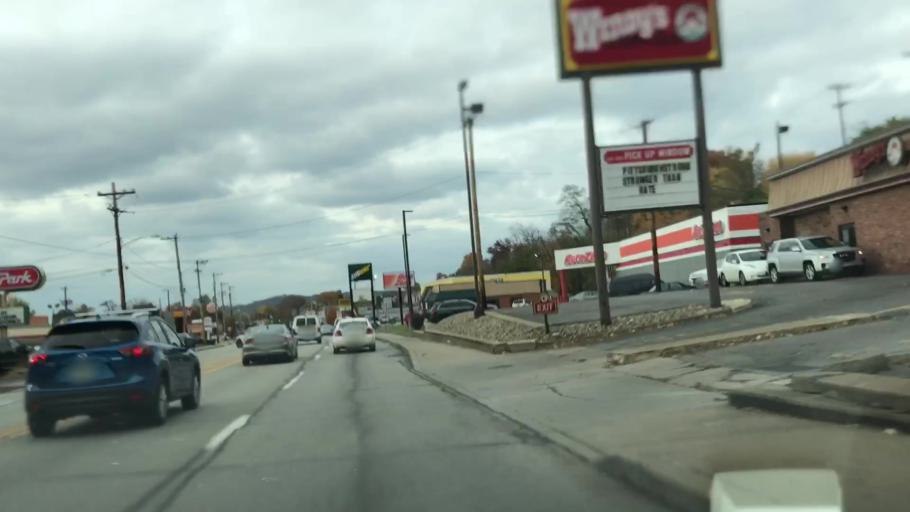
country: US
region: Pennsylvania
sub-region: Allegheny County
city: Avalon
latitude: 40.4939
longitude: -80.0637
